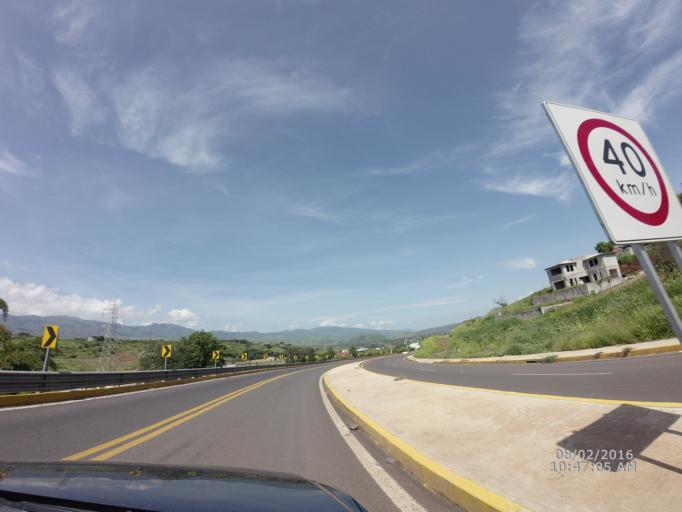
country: MX
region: Nayarit
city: Ixtlan del Rio
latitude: 21.0301
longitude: -104.3548
